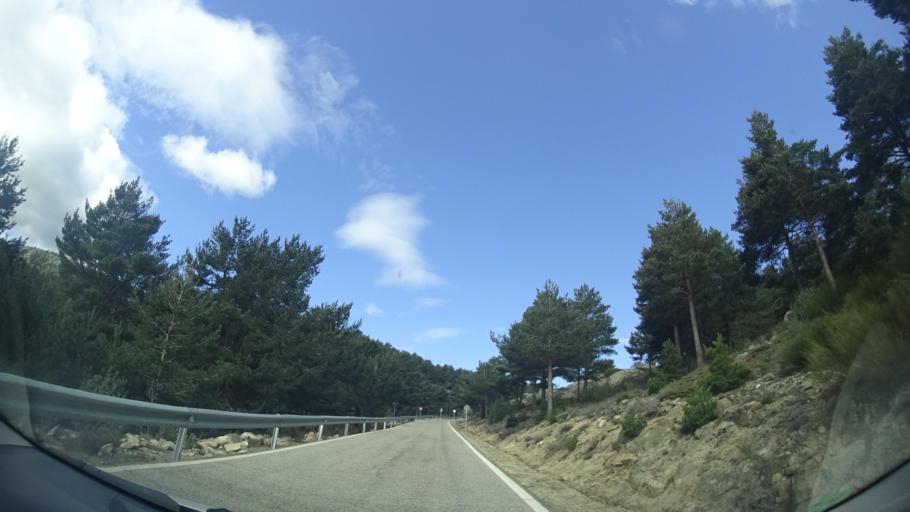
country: ES
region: Madrid
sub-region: Provincia de Madrid
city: Canencia
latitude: 40.8667
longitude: -3.7614
